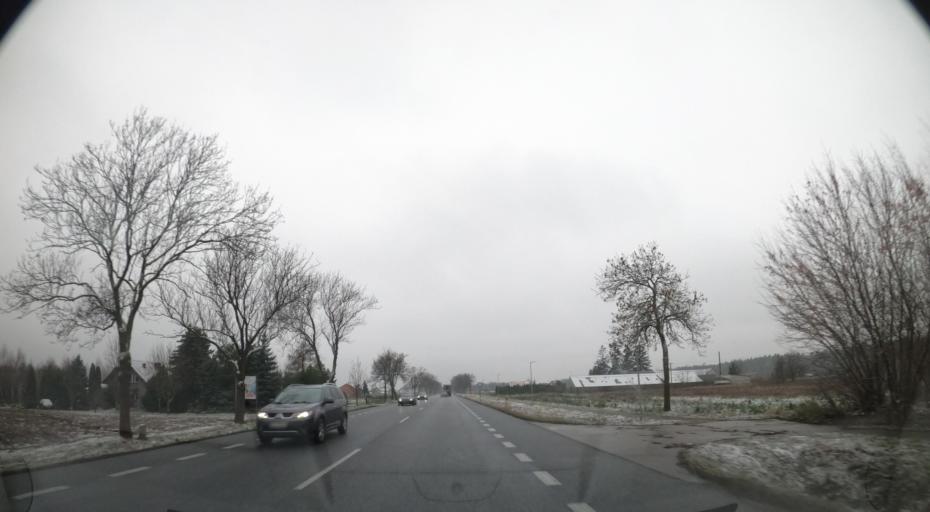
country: PL
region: Masovian Voivodeship
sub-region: Powiat sochaczewski
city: Sochaczew
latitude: 52.2235
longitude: 20.3035
